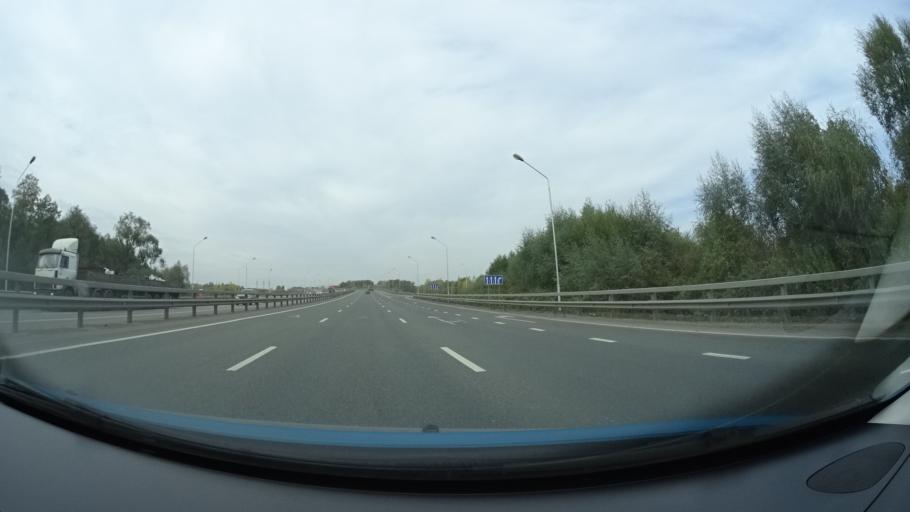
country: RU
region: Bashkortostan
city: Avdon
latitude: 54.6746
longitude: 55.8204
